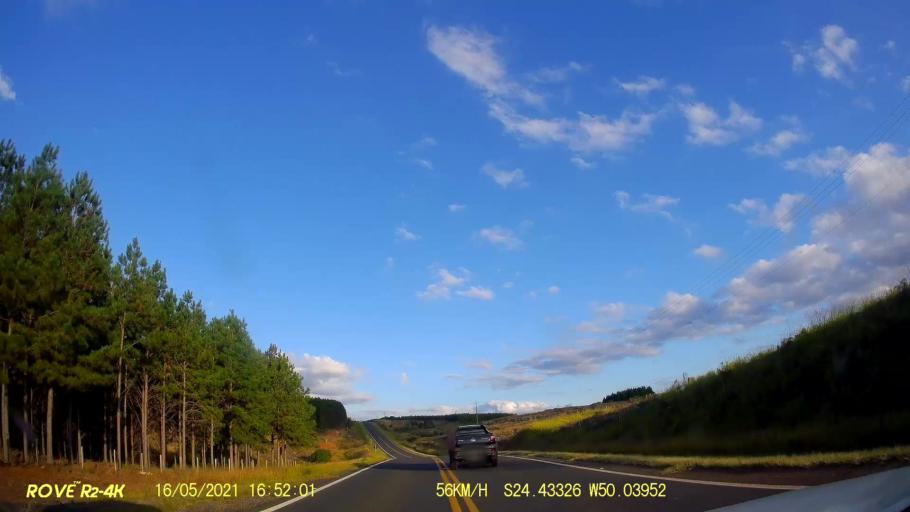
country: BR
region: Parana
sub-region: Pirai Do Sul
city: Pirai do Sul
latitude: -24.4333
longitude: -50.0395
